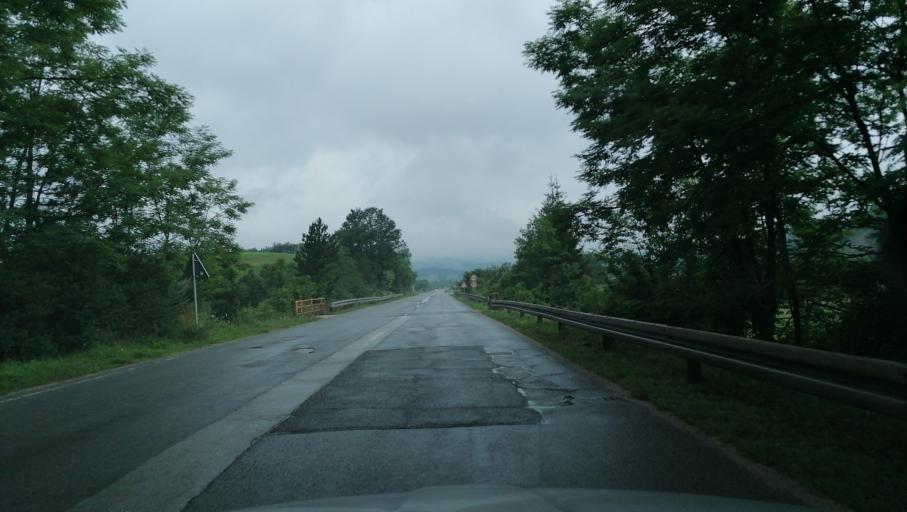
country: RS
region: Central Serbia
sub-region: Zlatiborski Okrug
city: Cajetina
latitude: 43.7901
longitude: 19.7069
